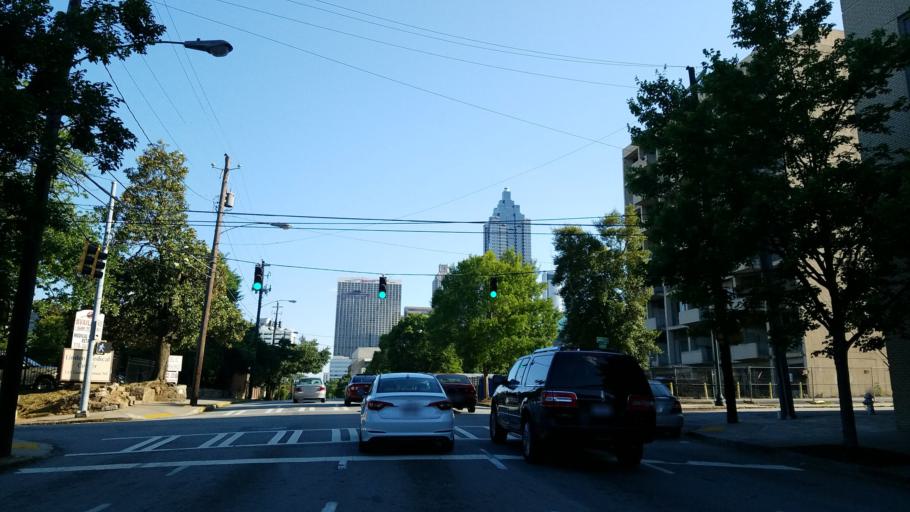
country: US
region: Georgia
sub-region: Fulton County
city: Atlanta
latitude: 33.7701
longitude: -84.3840
